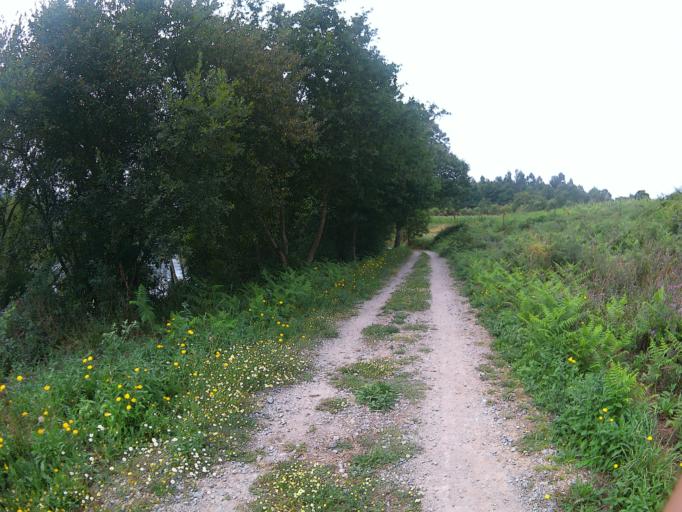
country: PT
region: Viana do Castelo
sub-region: Ponte de Lima
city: Ponte de Lima
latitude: 41.7922
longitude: -8.5150
